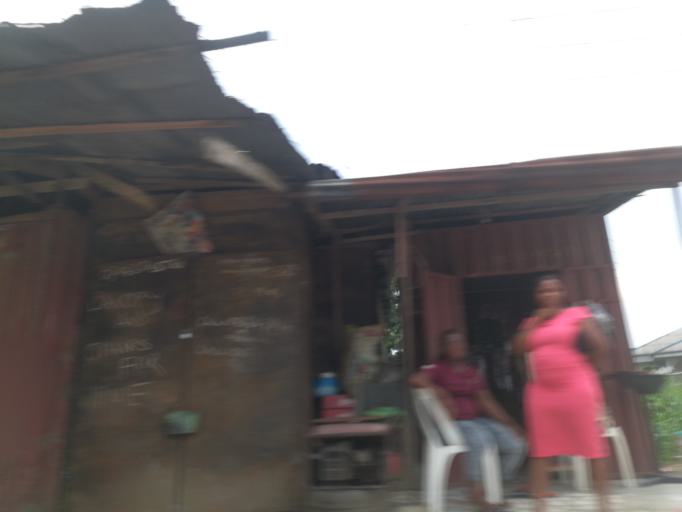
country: NG
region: Rivers
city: Okrika
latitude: 4.7844
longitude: 7.1289
